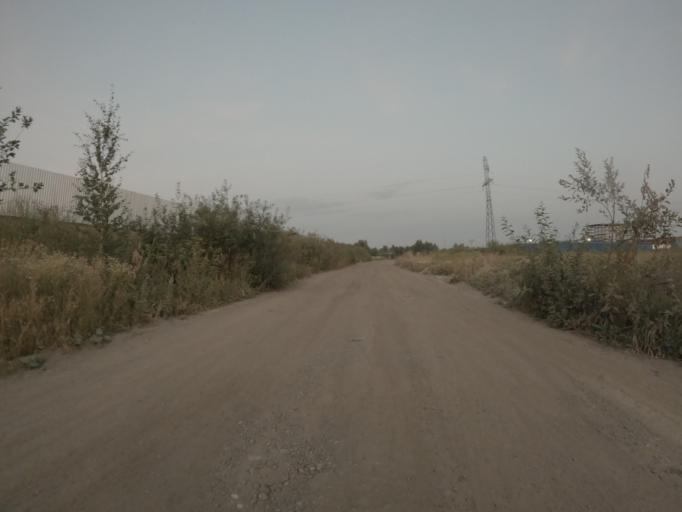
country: RU
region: Leningrad
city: Yanino Vtoroye
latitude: 59.9354
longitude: 30.5953
